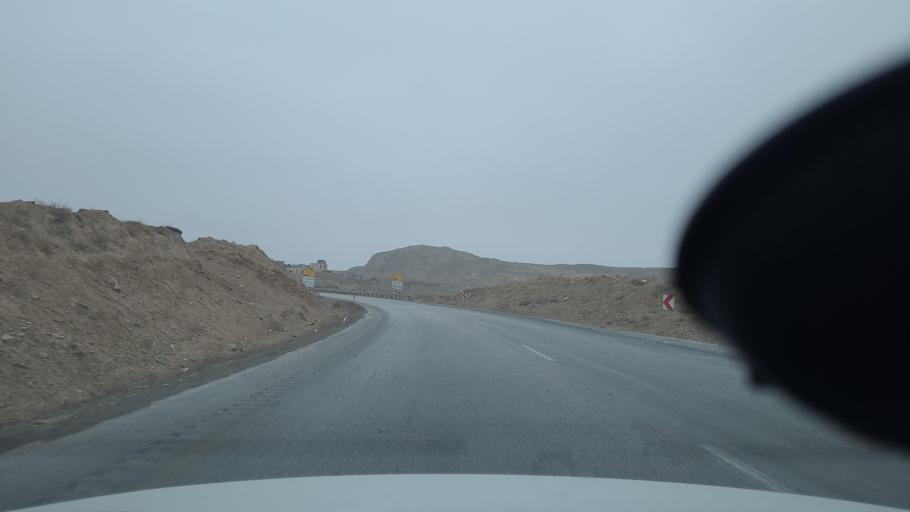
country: IR
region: Razavi Khorasan
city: Fariman
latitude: 35.9906
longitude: 59.7417
